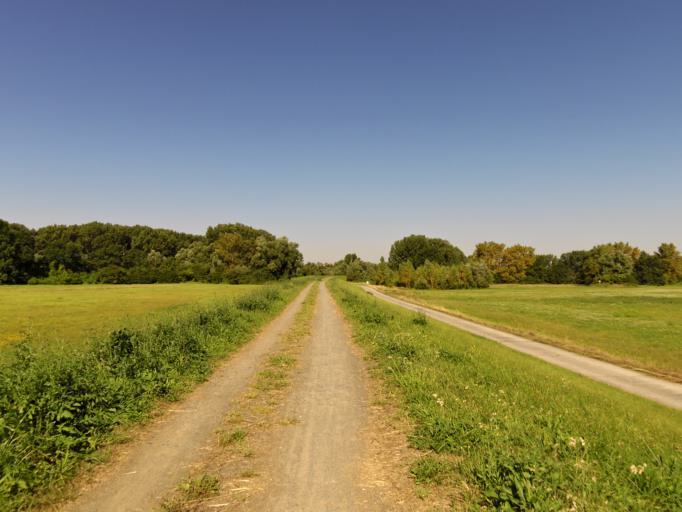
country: DE
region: Rheinland-Pfalz
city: Oppenheim
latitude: 49.8532
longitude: 8.3951
